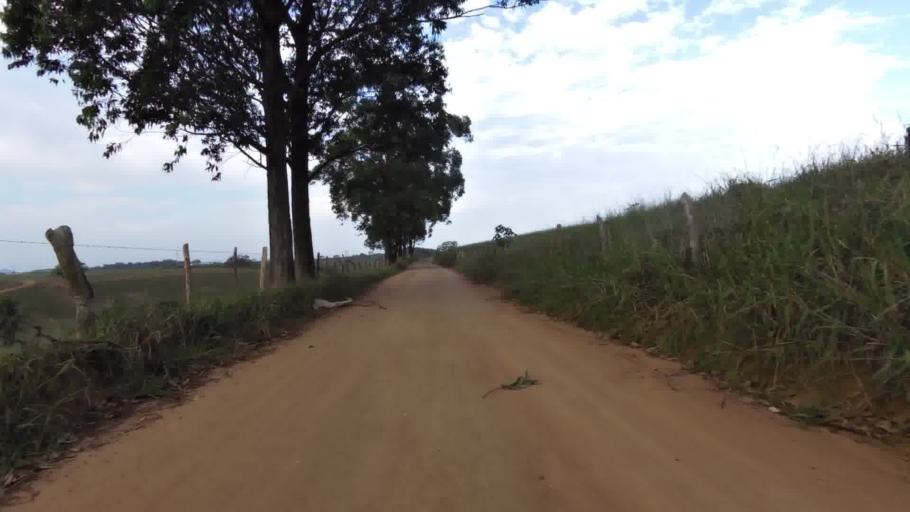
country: BR
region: Espirito Santo
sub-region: Piuma
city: Piuma
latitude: -20.8344
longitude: -40.7465
